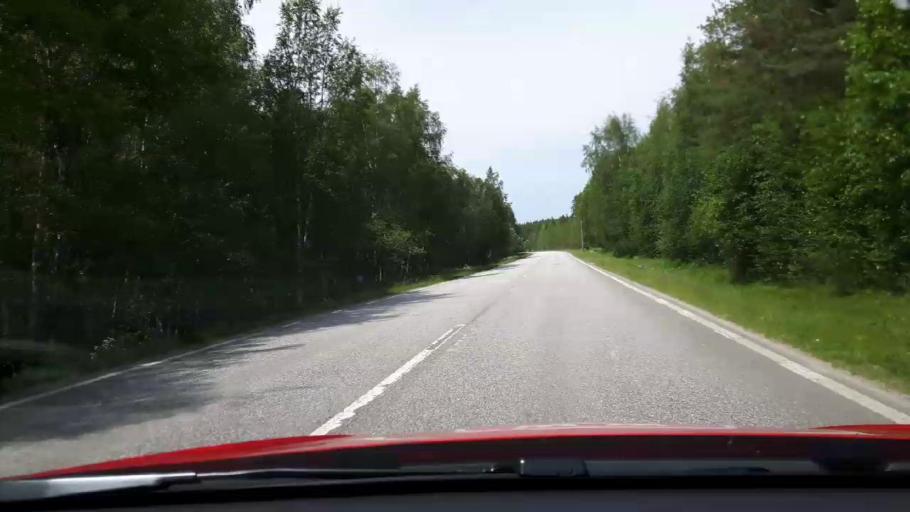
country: SE
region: Jaemtland
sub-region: Harjedalens Kommun
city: Sveg
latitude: 62.1314
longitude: 14.0568
